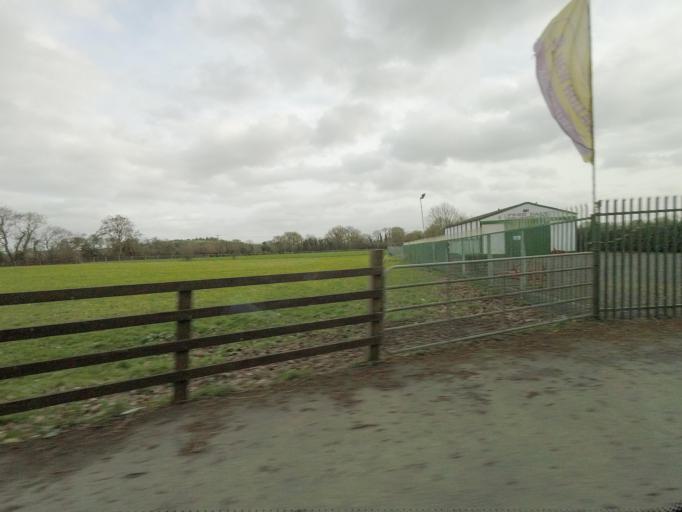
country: IE
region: Leinster
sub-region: Kildare
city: Naas
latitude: 53.1681
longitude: -6.6880
